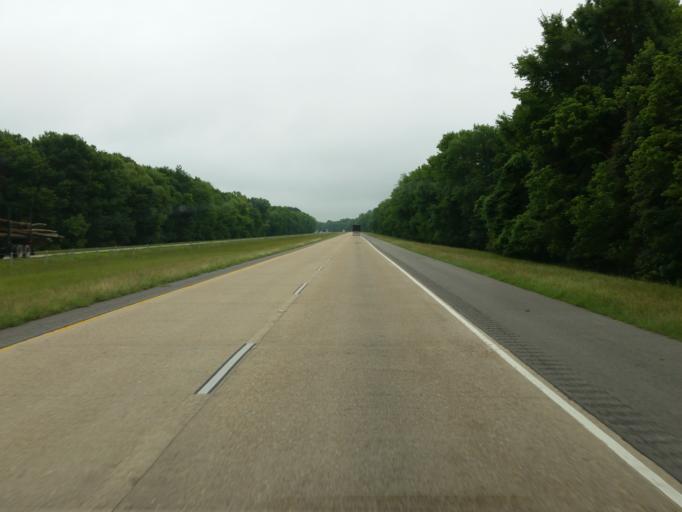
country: US
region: Louisiana
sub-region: Madison Parish
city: Tallulah
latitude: 32.3421
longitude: -91.0743
